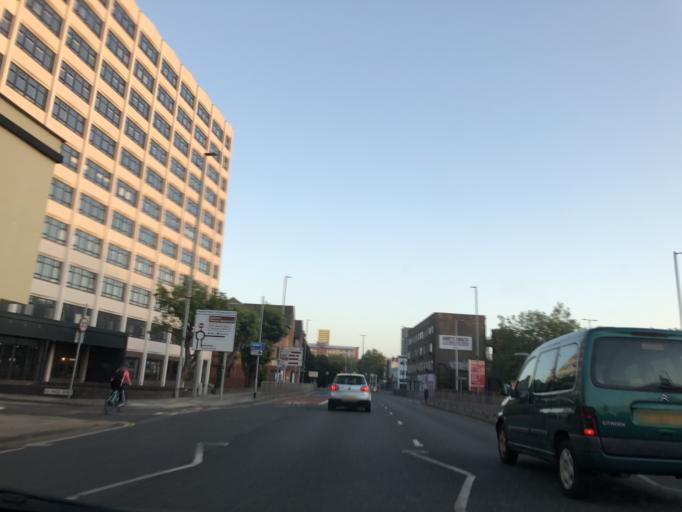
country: GB
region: England
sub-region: Portsmouth
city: Portsmouth
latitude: 50.8049
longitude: -1.0868
